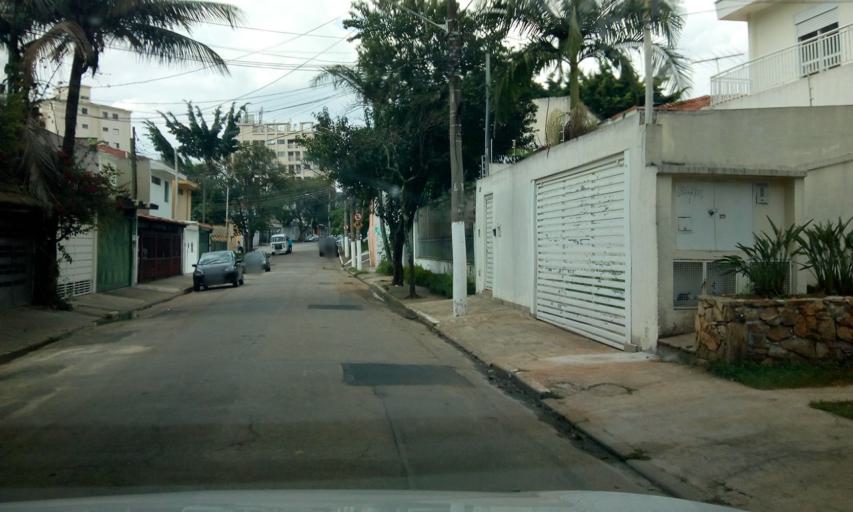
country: BR
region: Sao Paulo
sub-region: Diadema
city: Diadema
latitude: -23.6213
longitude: -46.6647
